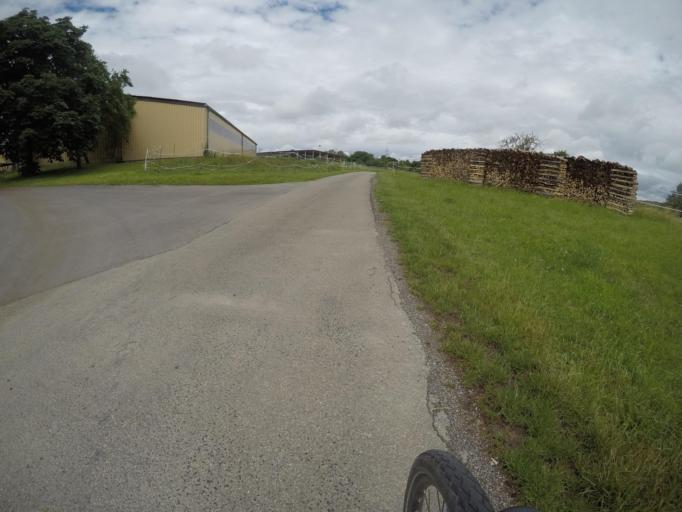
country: DE
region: Baden-Wuerttemberg
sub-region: Regierungsbezirk Stuttgart
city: Gartringen
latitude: 48.6459
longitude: 8.8842
